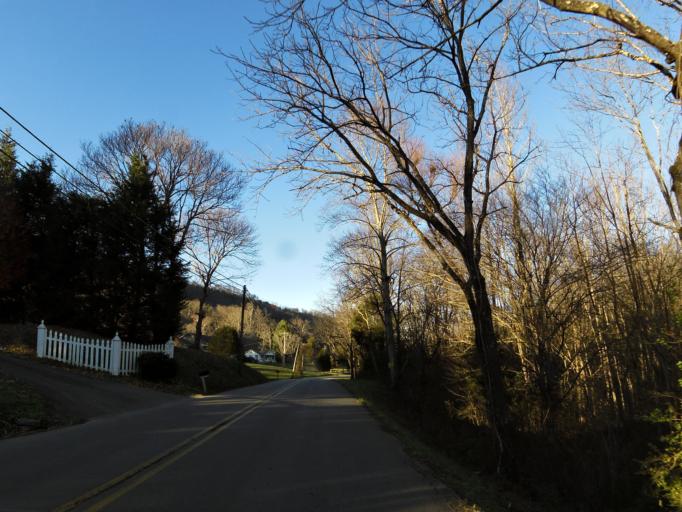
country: US
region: Tennessee
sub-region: Anderson County
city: Rocky Top
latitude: 36.1802
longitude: -84.1609
